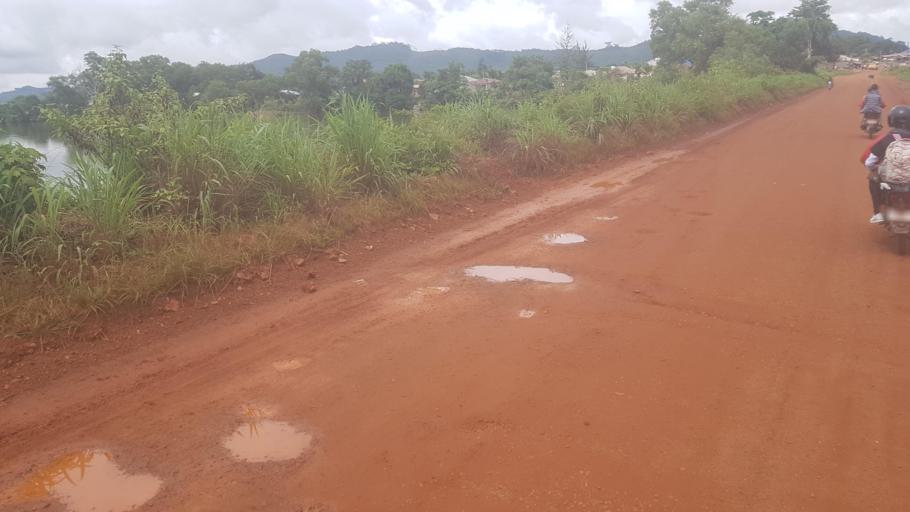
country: SL
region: Southern Province
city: Mogbwemo
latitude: 7.7644
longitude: -12.3032
